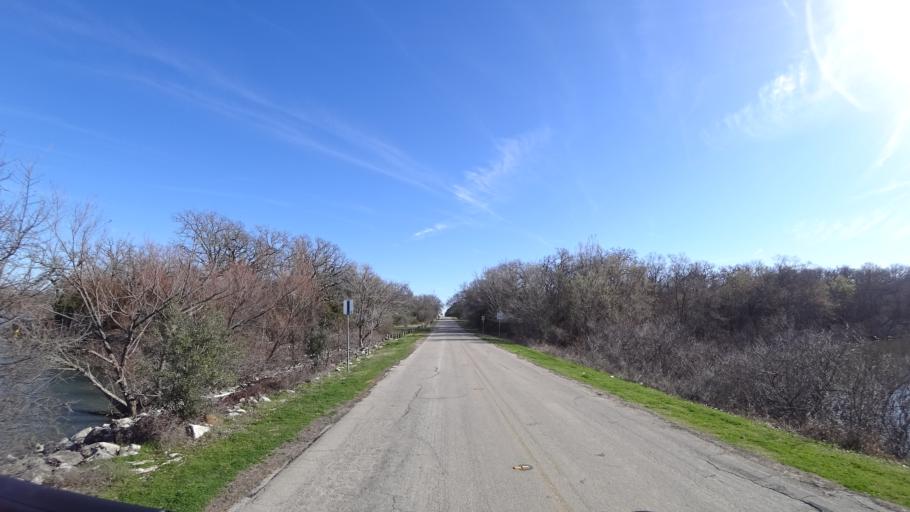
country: US
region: Texas
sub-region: Denton County
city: Highland Village
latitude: 33.0806
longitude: -97.0152
